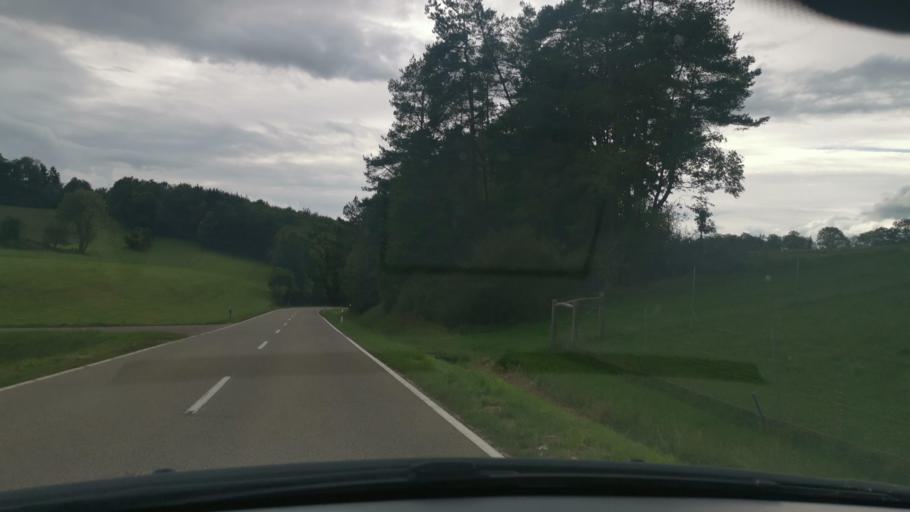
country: DE
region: Baden-Wuerttemberg
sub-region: Tuebingen Region
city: Hayingen
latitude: 48.3062
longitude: 9.5282
